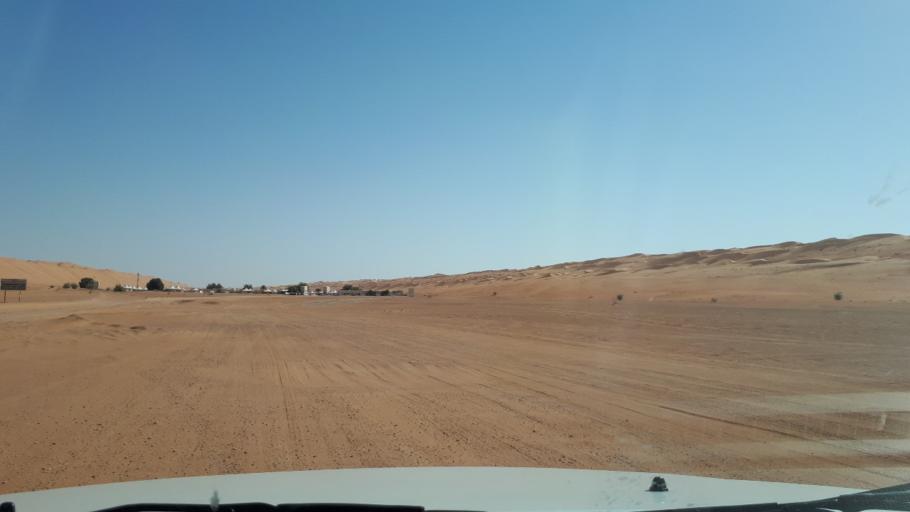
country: OM
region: Ash Sharqiyah
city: Badiyah
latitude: 22.4054
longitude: 58.7240
